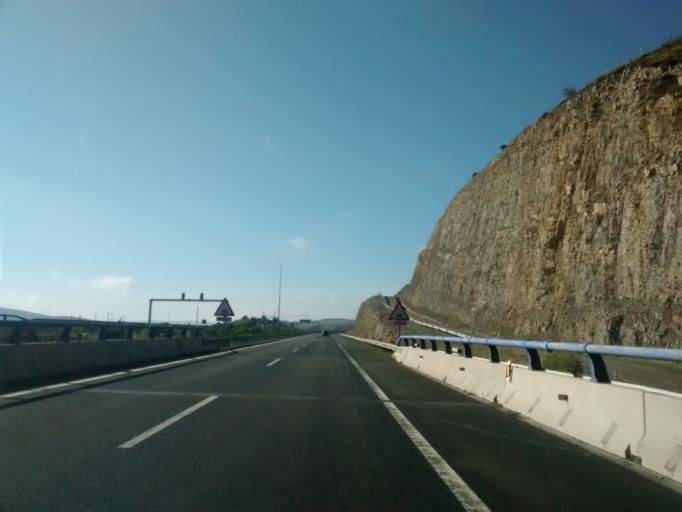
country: ES
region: Cantabria
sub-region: Provincia de Cantabria
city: Santiurde de Reinosa
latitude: 43.0433
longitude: -4.0888
